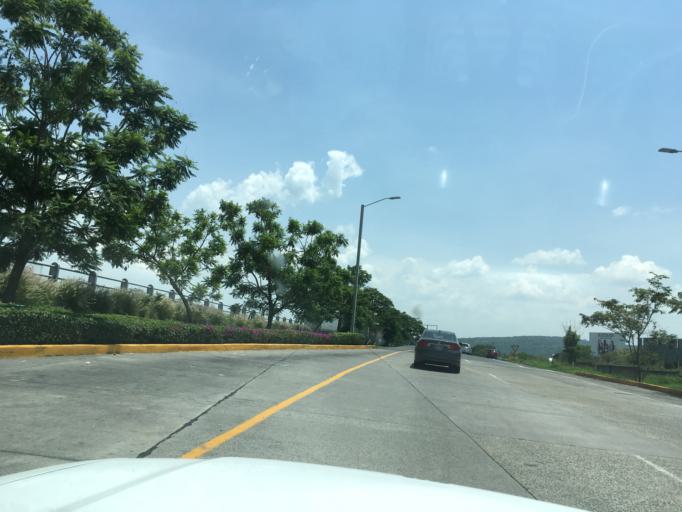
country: MX
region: Jalisco
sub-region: Tonala
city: Mismaloya (Fraccionamiento Pedregal de Santa Martha)
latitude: 20.6046
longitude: -103.1401
